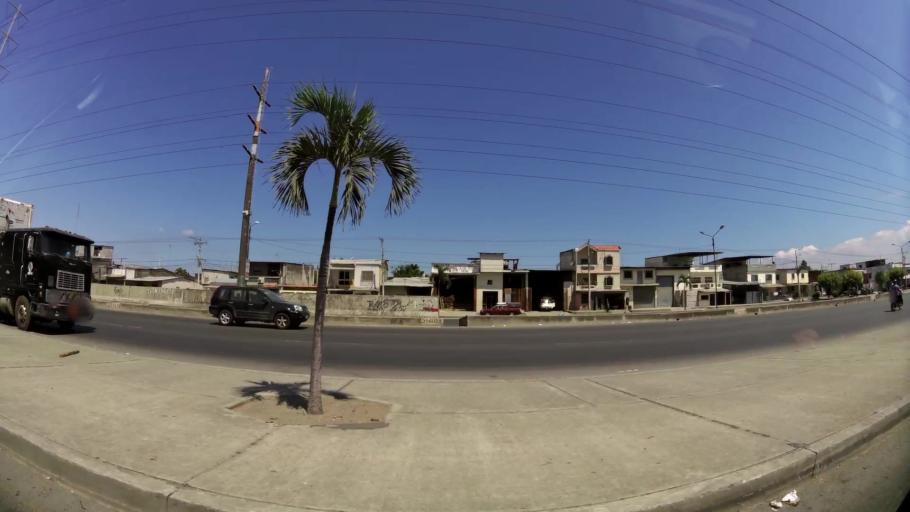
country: EC
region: Guayas
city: Guayaquil
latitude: -2.2392
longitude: -79.9225
